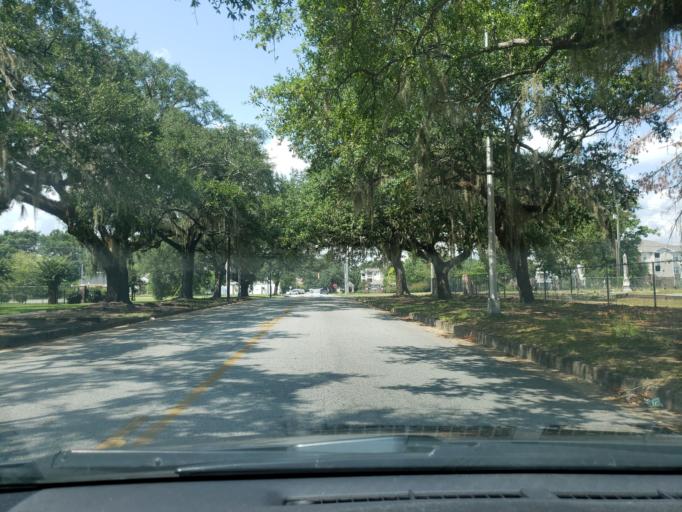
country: US
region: Georgia
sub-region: Dougherty County
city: Albany
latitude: 31.5708
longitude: -84.1536
